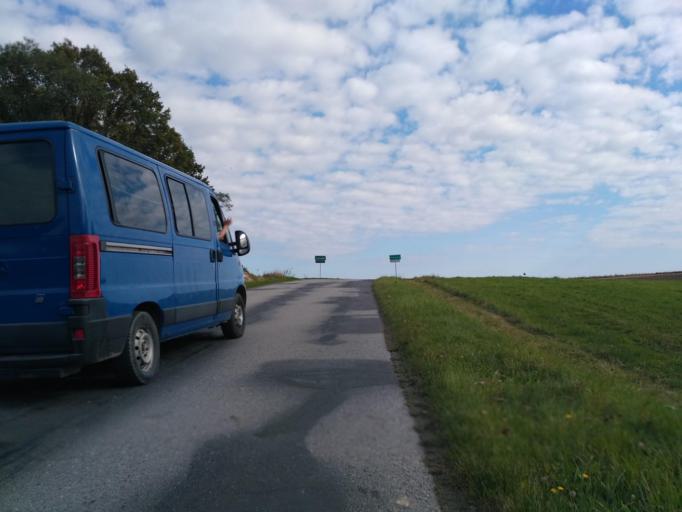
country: PL
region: Subcarpathian Voivodeship
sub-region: Powiat debicki
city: Brzostek
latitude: 49.8912
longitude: 21.3464
